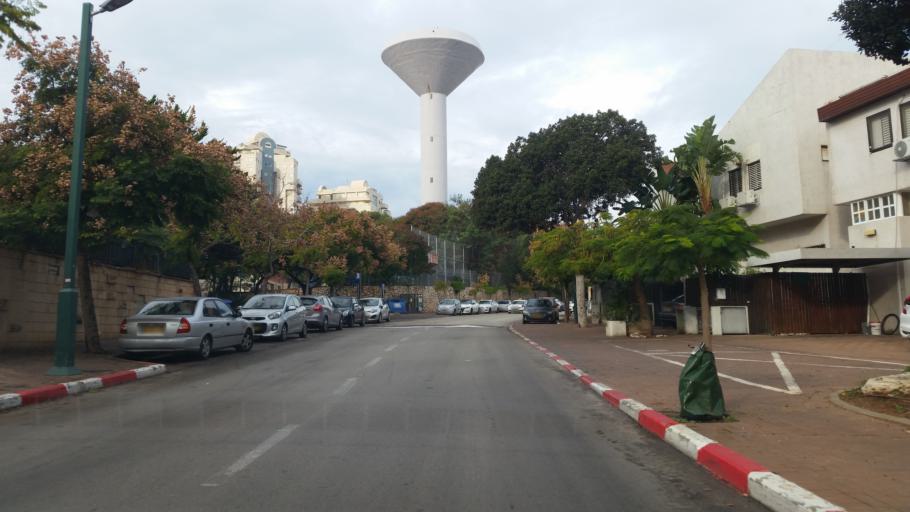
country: IL
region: Tel Aviv
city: Ramat HaSharon
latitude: 32.1510
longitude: 34.8497
